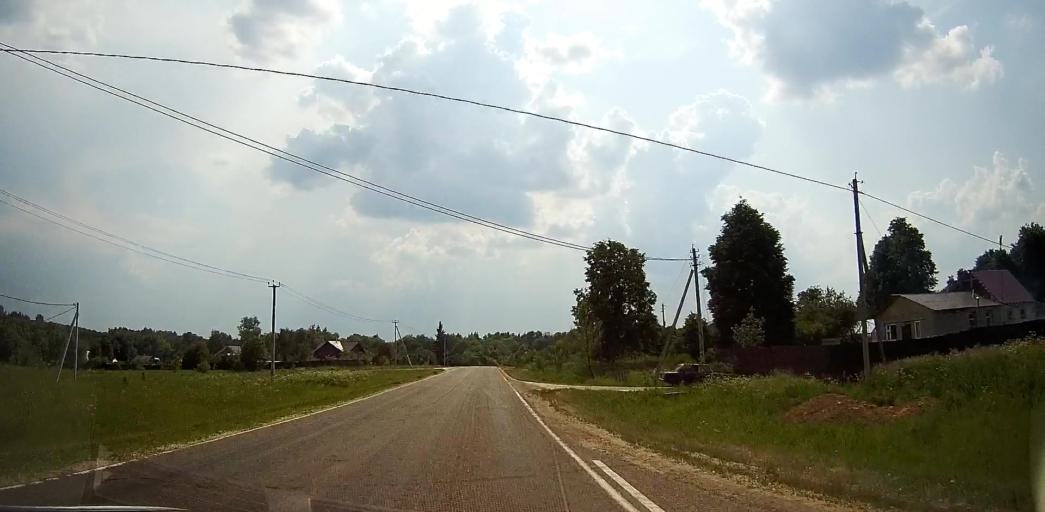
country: RU
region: Moskovskaya
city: Zhilevo
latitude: 55.0580
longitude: 38.0848
